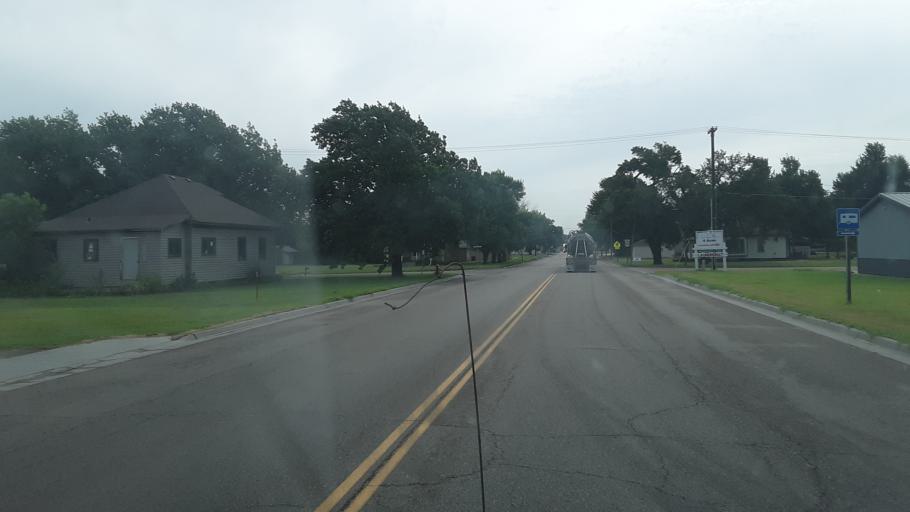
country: US
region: Kansas
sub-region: Edwards County
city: Kinsley
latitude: 37.9188
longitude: -99.4149
